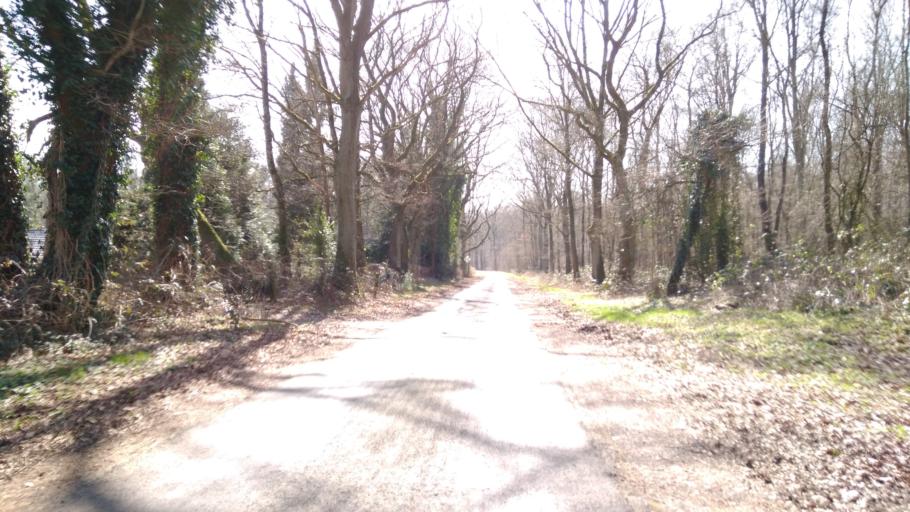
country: DE
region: North Rhine-Westphalia
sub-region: Regierungsbezirk Munster
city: Bottrop
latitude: 51.5837
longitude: 6.9265
